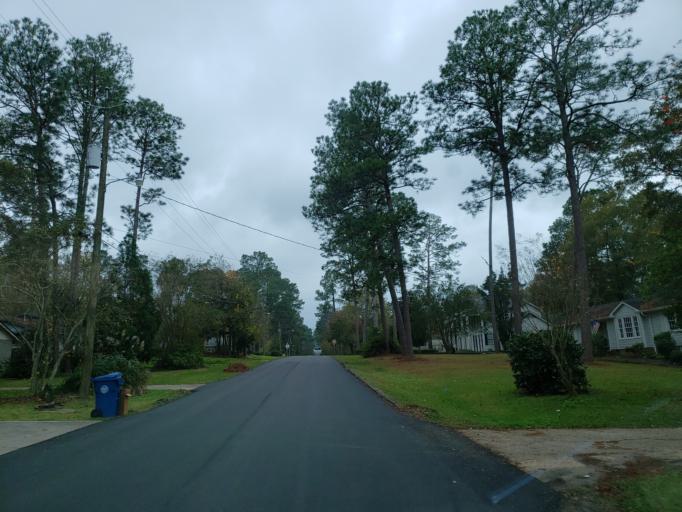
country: US
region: Mississippi
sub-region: Forrest County
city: Hattiesburg
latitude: 31.3163
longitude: -89.3228
